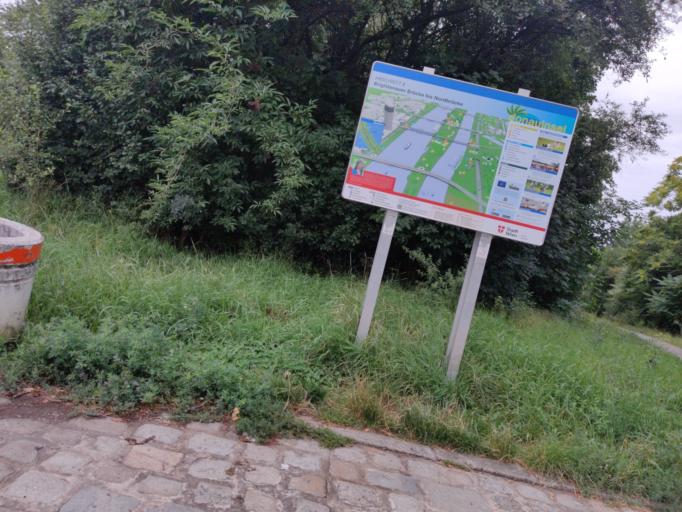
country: AT
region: Vienna
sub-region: Wien Stadt
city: Vienna
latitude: 48.2499
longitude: 16.3865
